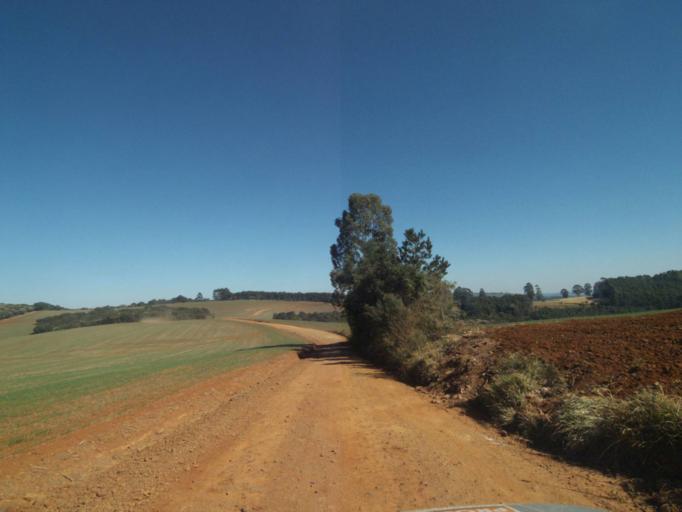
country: BR
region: Parana
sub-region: Tibagi
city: Tibagi
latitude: -24.5630
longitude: -50.6251
